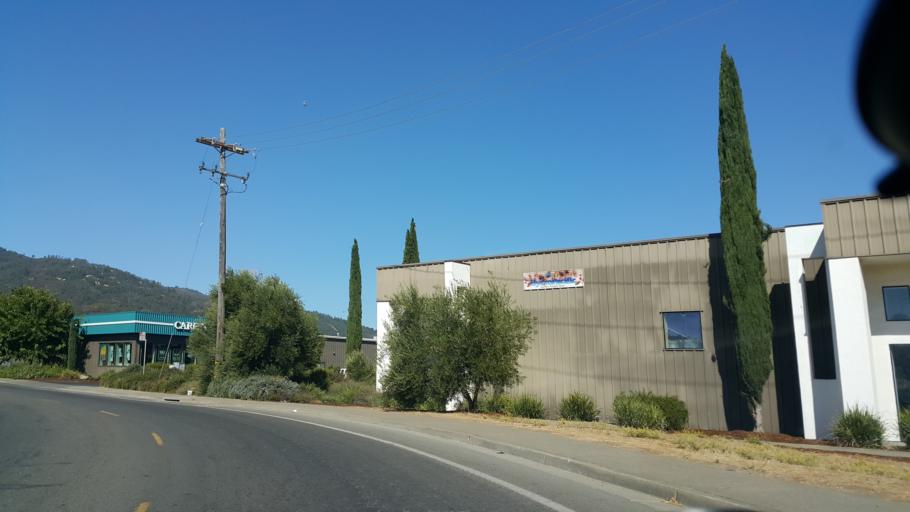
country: US
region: California
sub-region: Mendocino County
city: Ukiah
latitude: 39.1340
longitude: -123.2009
